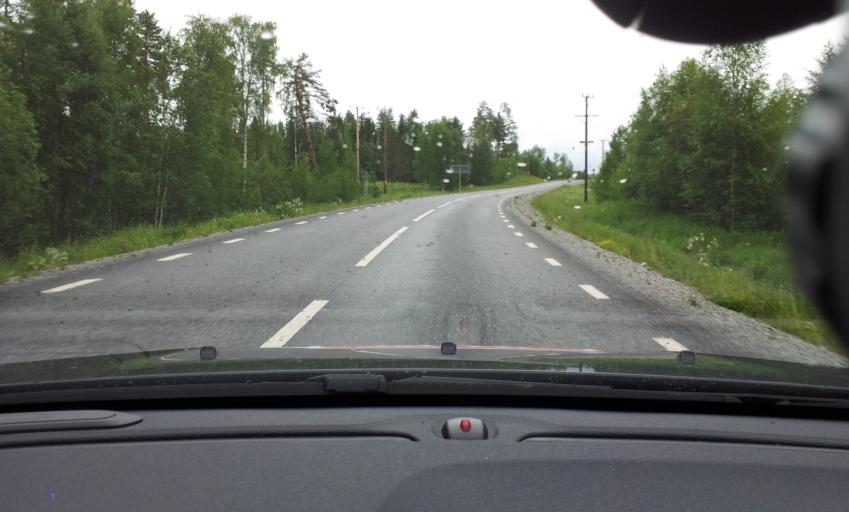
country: SE
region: Jaemtland
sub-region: OEstersunds Kommun
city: Lit
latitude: 63.7360
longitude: 14.7440
